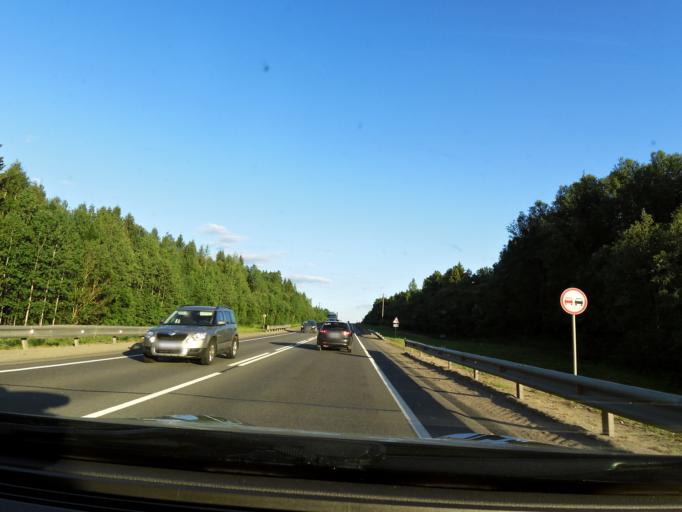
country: RU
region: Vologda
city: Vologda
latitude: 59.1361
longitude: 39.9531
